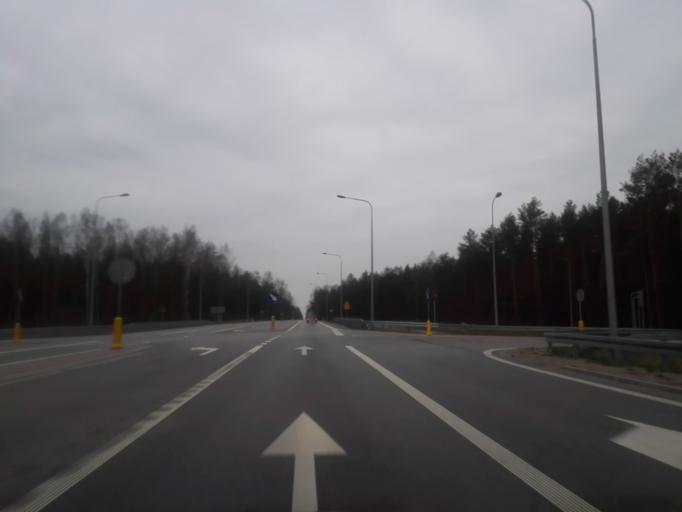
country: PL
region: Podlasie
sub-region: Powiat kolnenski
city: Stawiski
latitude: 53.3532
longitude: 22.1605
